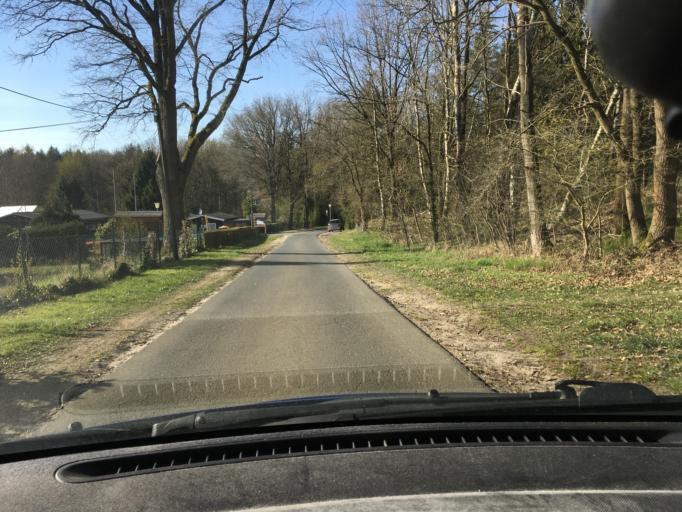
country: DE
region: Lower Saxony
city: Amelinghausen
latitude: 53.1215
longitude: 10.2304
